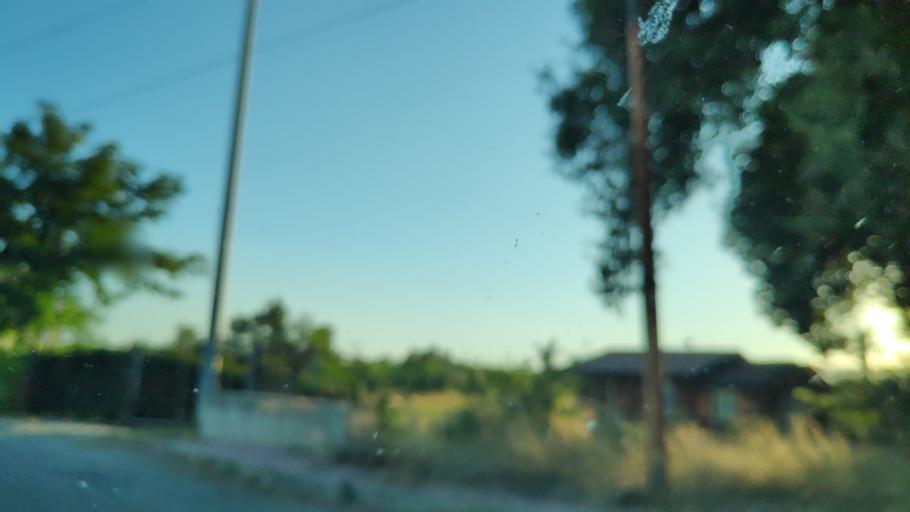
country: IT
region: Calabria
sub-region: Provincia di Reggio Calabria
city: Monasterace Marina
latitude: 38.4340
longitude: 16.5641
